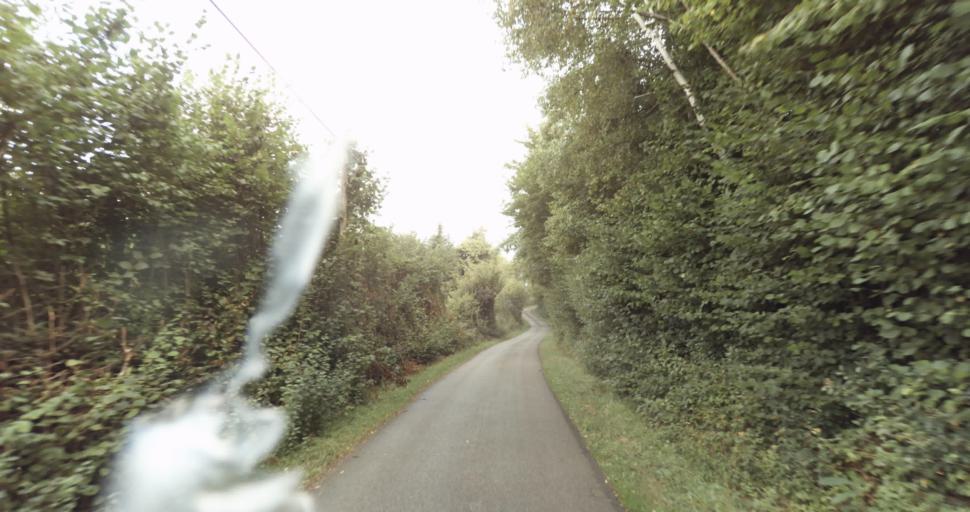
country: FR
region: Lower Normandy
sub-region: Departement de l'Orne
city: Gace
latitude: 48.8565
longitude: 0.2988
